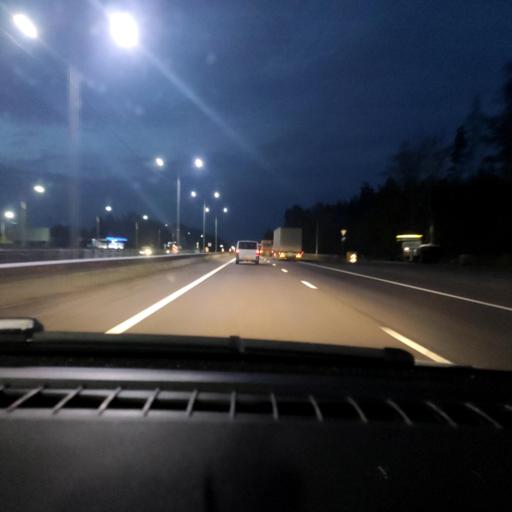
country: RU
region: Voronezj
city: Ramon'
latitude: 51.8968
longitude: 39.2185
